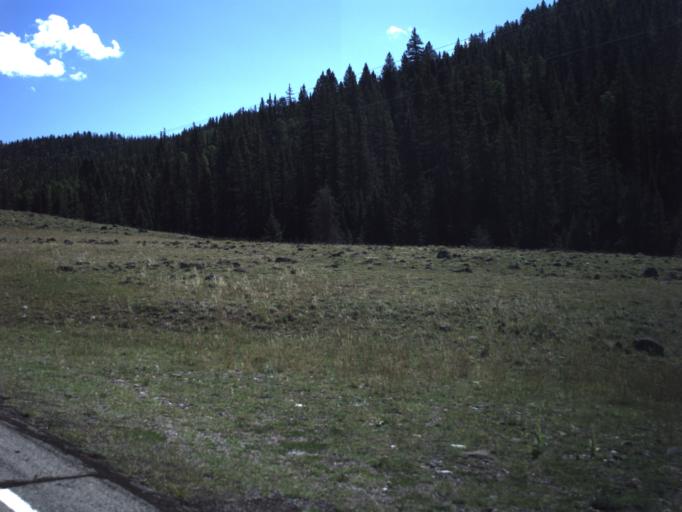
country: US
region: Utah
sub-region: Beaver County
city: Beaver
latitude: 38.3011
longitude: -112.4315
